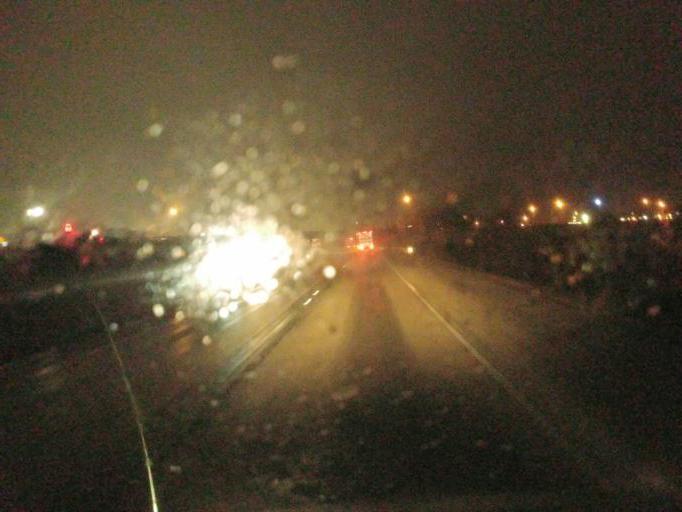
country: US
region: Illinois
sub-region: Fayette County
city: Vandalia
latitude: 38.9782
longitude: -89.0942
